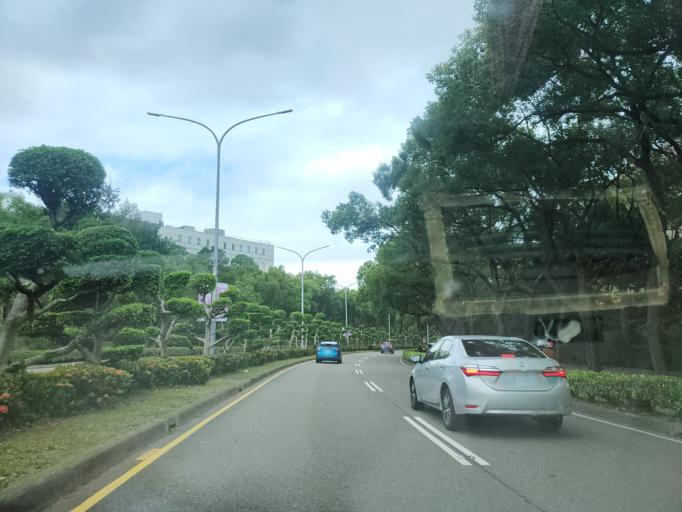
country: TW
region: Taiwan
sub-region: Hsinchu
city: Hsinchu
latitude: 24.7788
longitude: 121.0069
